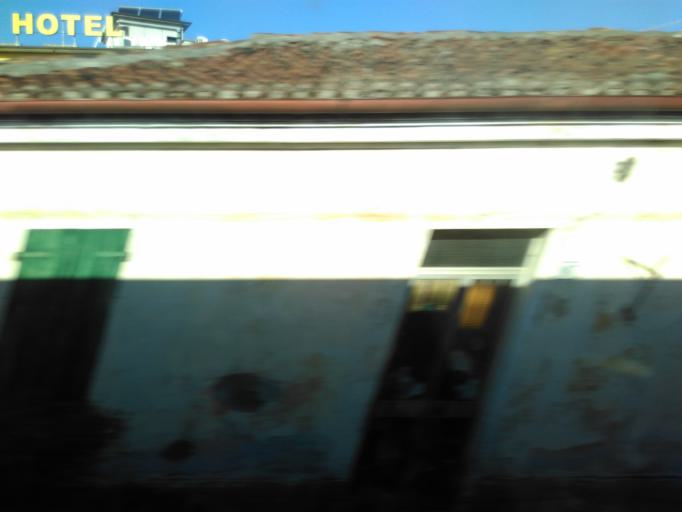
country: IT
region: Veneto
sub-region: Provincia di Verona
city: Lugagnano
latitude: 45.4274
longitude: 10.8951
